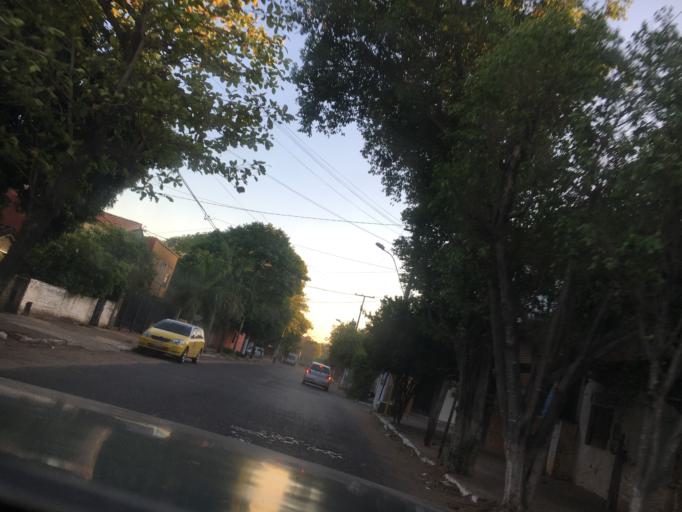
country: PY
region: Central
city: Lambare
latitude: -25.3206
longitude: -57.6104
